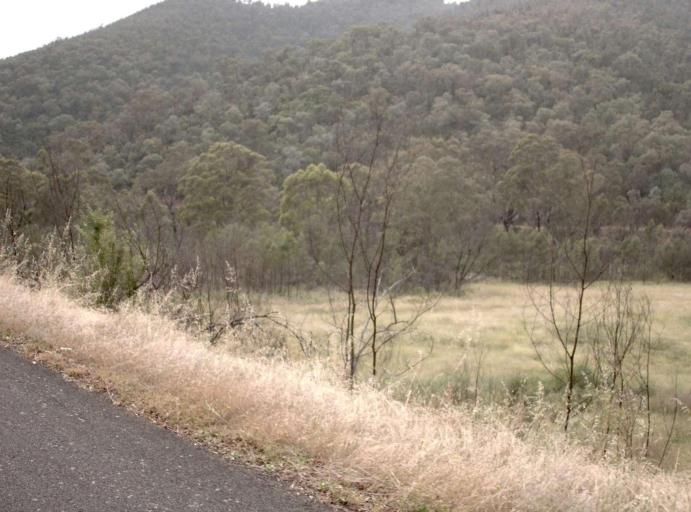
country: AU
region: Victoria
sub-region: Wellington
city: Heyfield
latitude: -37.7437
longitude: 146.6665
